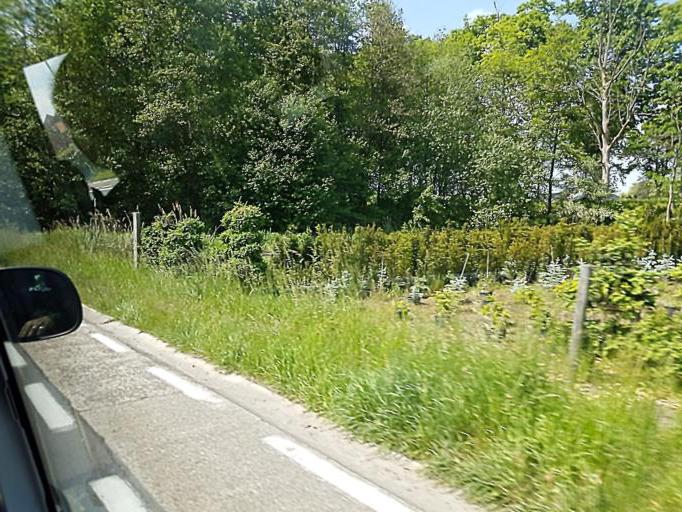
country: BE
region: Flanders
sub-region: Provincie Limburg
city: Neerpelt
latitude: 51.2310
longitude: 5.4556
